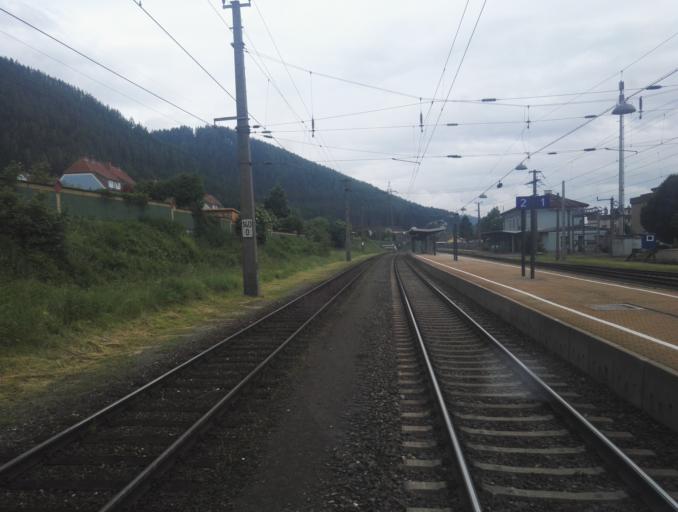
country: AT
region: Styria
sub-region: Politischer Bezirk Bruck-Muerzzuschlag
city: Kindberg
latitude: 47.5019
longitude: 15.4493
